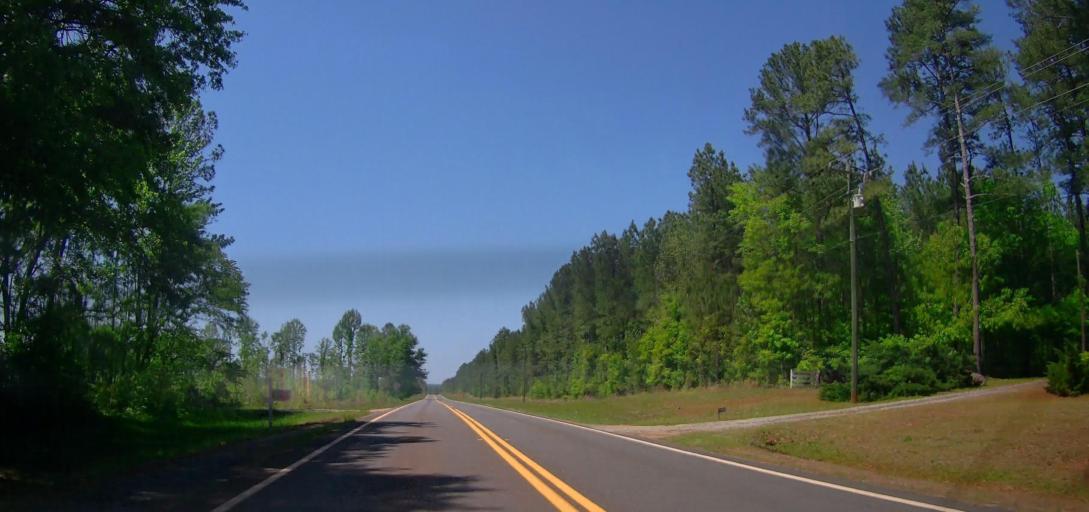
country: US
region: Georgia
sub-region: Jasper County
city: Monticello
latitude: 33.2545
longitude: -83.5665
